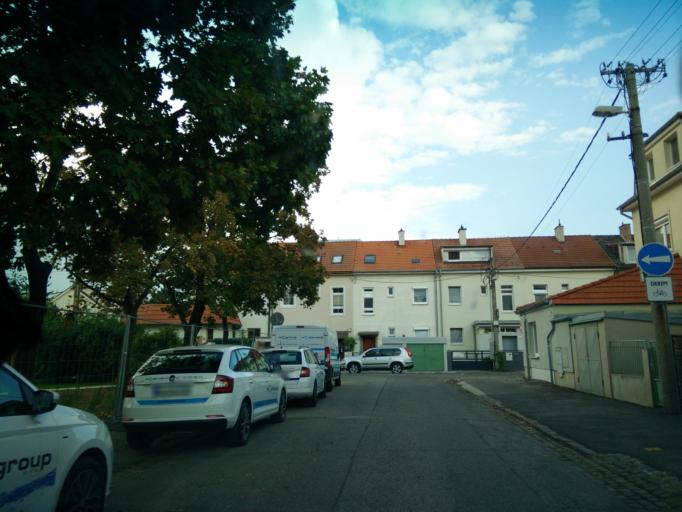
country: SK
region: Bratislavsky
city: Bratislava
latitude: 48.1694
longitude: 17.1346
